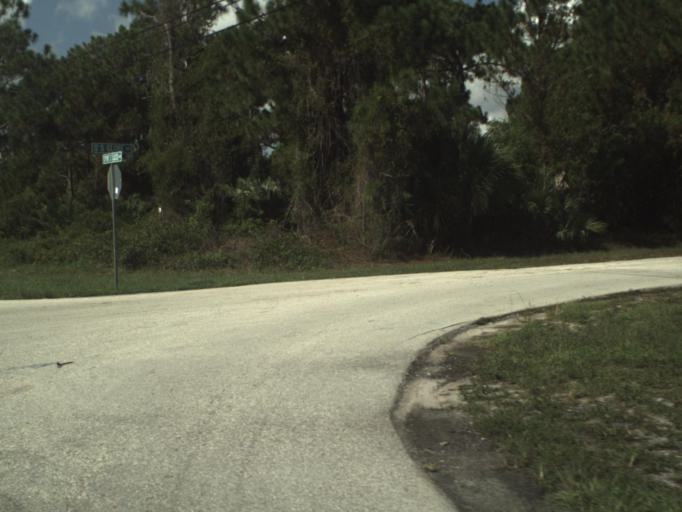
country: US
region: Florida
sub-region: Saint Lucie County
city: Port Saint Lucie
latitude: 27.2448
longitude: -80.3769
